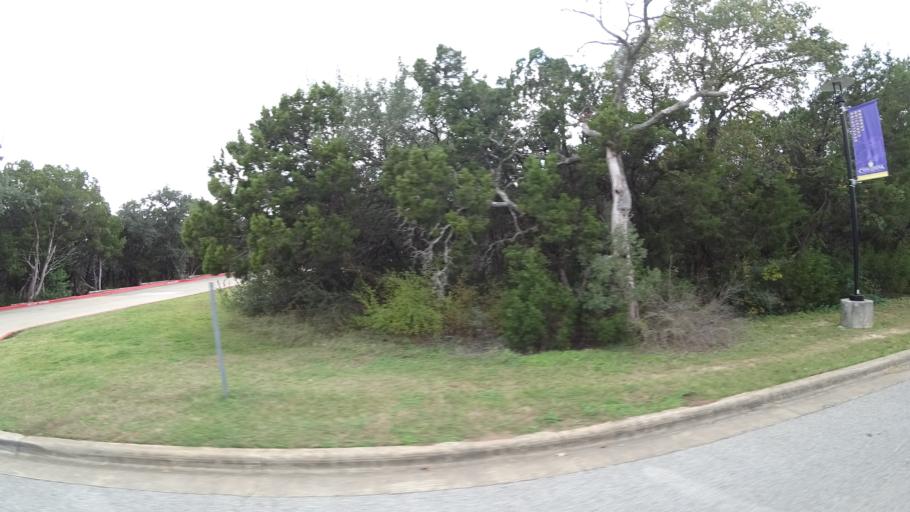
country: US
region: Texas
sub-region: Williamson County
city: Anderson Mill
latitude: 30.4216
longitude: -97.8439
